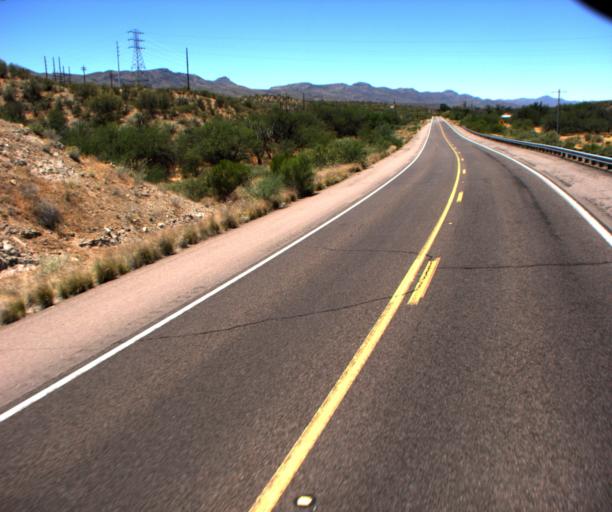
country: US
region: Arizona
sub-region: Pinal County
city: Kearny
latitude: 33.0897
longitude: -110.7169
